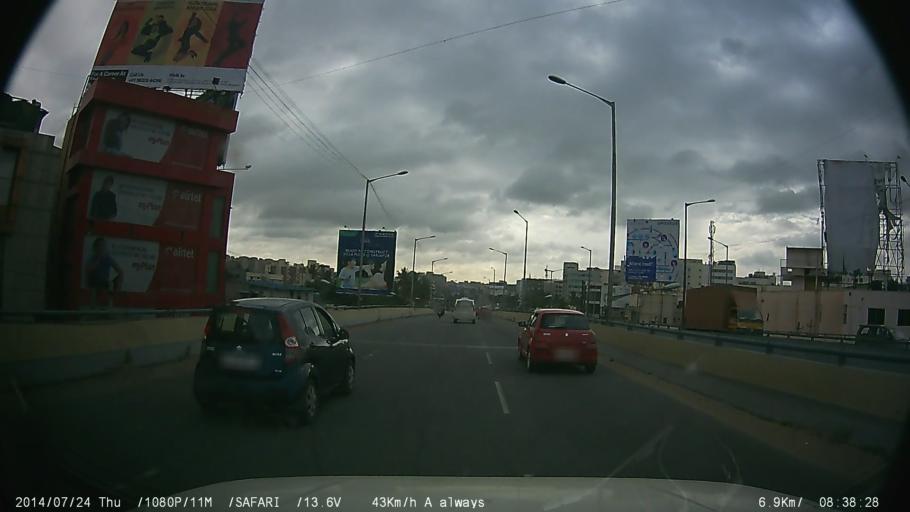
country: IN
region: Karnataka
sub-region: Bangalore Urban
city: Bangalore
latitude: 12.9263
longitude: 77.6770
